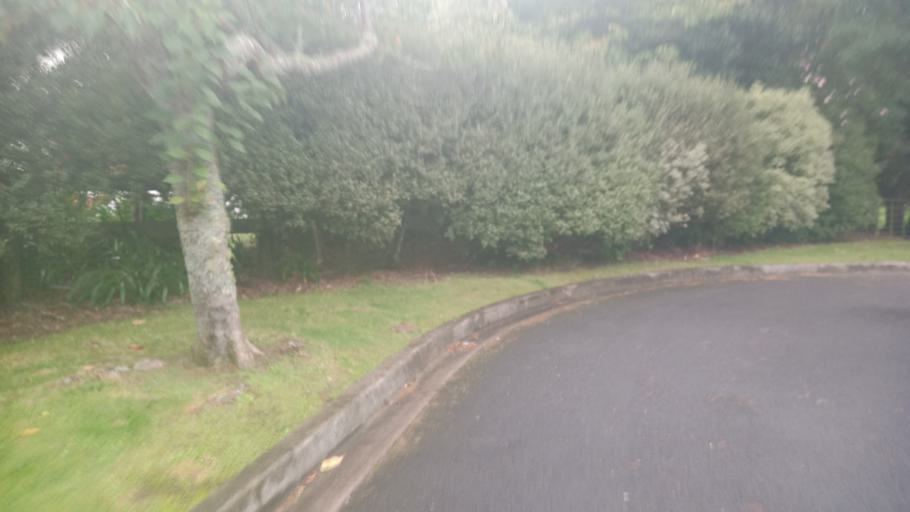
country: NZ
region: Gisborne
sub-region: Gisborne District
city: Gisborne
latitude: -38.6616
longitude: 178.0518
